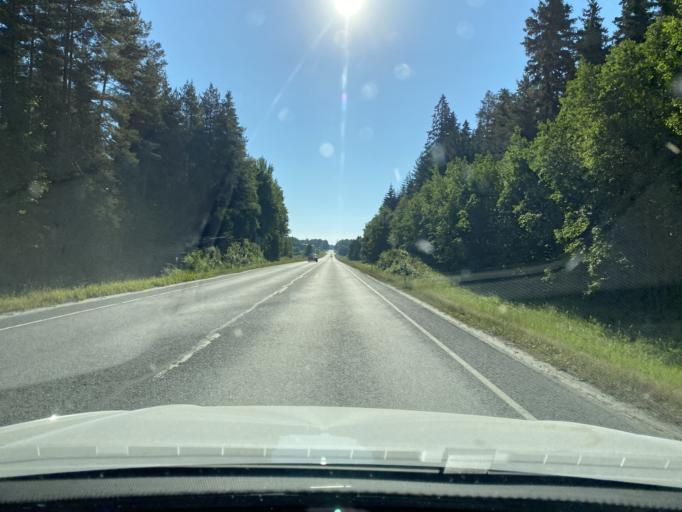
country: FI
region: Haeme
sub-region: Forssa
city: Forssa
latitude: 60.8297
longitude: 23.6789
